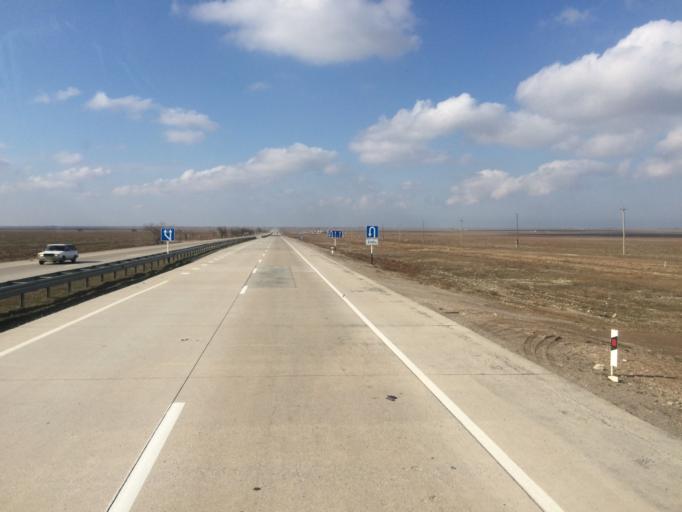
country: KZ
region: Ongtustik Qazaqstan
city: Temirlanovka
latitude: 42.8324
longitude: 69.1242
